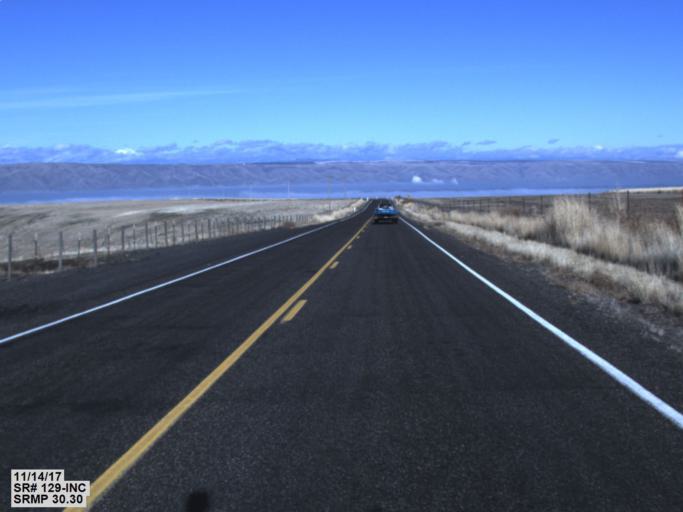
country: US
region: Washington
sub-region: Asotin County
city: Asotin
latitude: 46.2955
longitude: -117.0452
